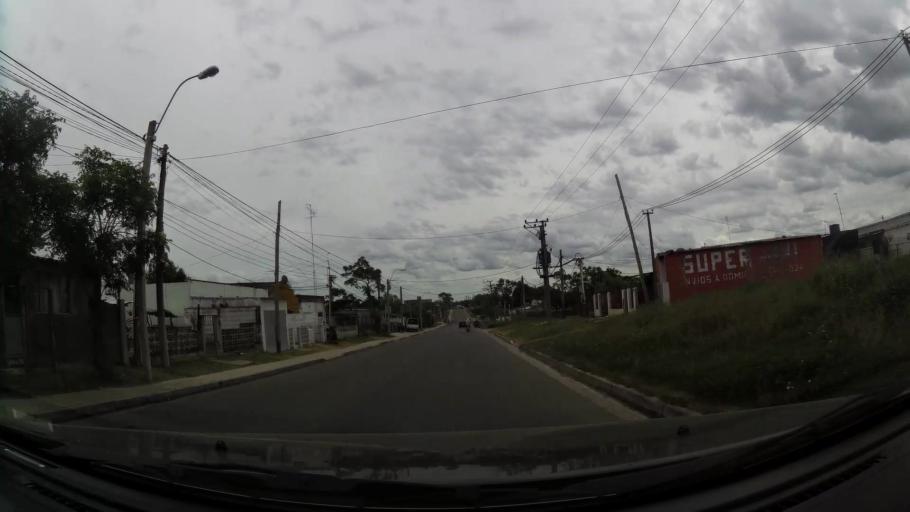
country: UY
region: Canelones
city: Las Piedras
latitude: -34.7202
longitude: -56.2096
